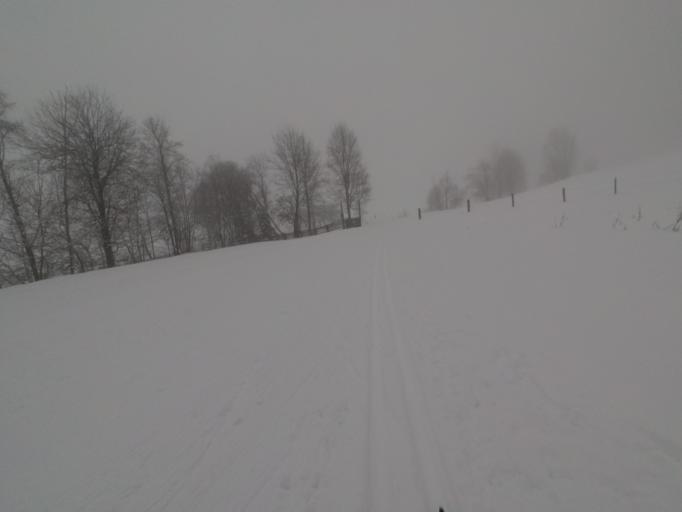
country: AT
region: Salzburg
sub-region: Politischer Bezirk Sankt Johann im Pongau
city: Wagrain
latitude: 47.3471
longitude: 13.3119
